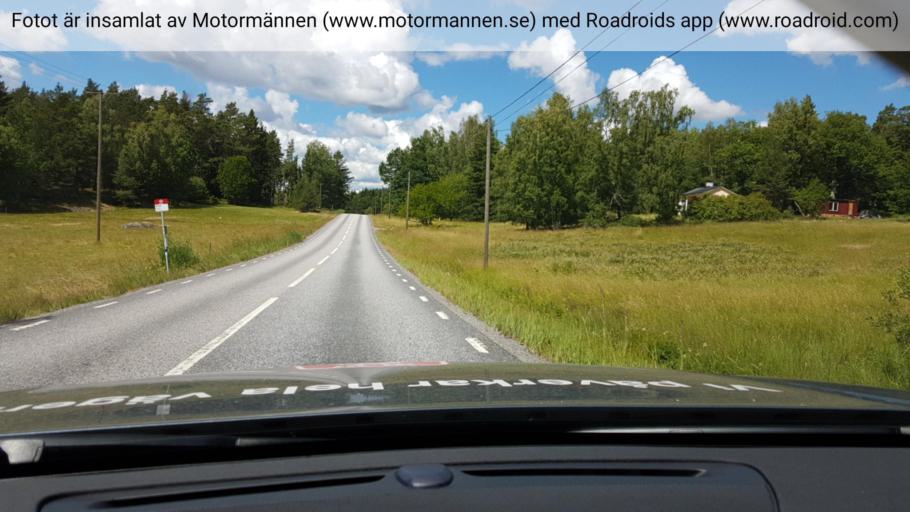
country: SE
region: Stockholm
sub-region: Varmdo Kommun
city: Hemmesta
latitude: 59.3937
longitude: 18.4853
